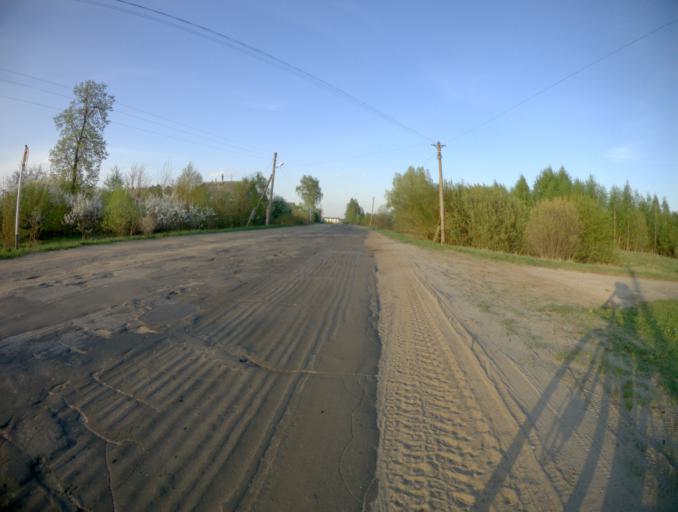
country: RU
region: Ivanovo
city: Yuzha
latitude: 56.5760
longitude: 41.9766
